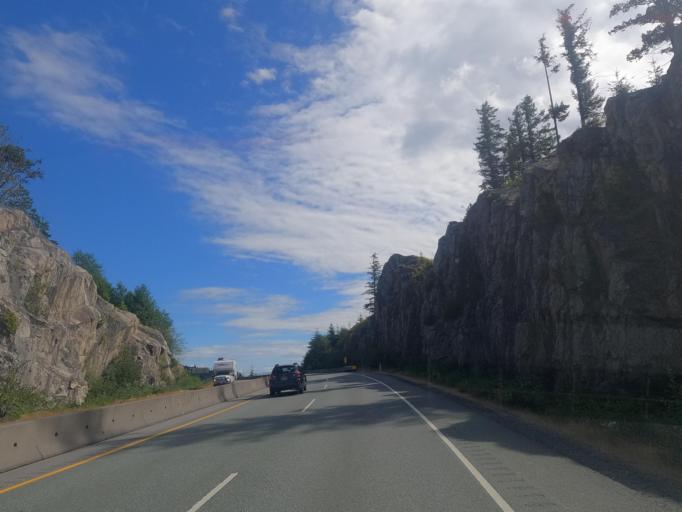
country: CA
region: British Columbia
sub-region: Greater Vancouver Regional District
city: Bowen Island
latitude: 49.3632
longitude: -123.2740
